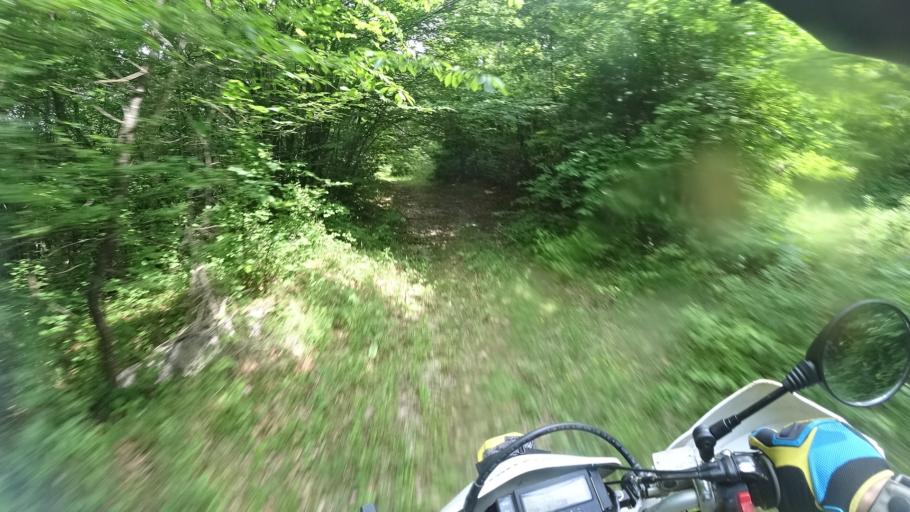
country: BA
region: Federation of Bosnia and Herzegovina
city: Izacic
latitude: 44.8729
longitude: 15.7039
